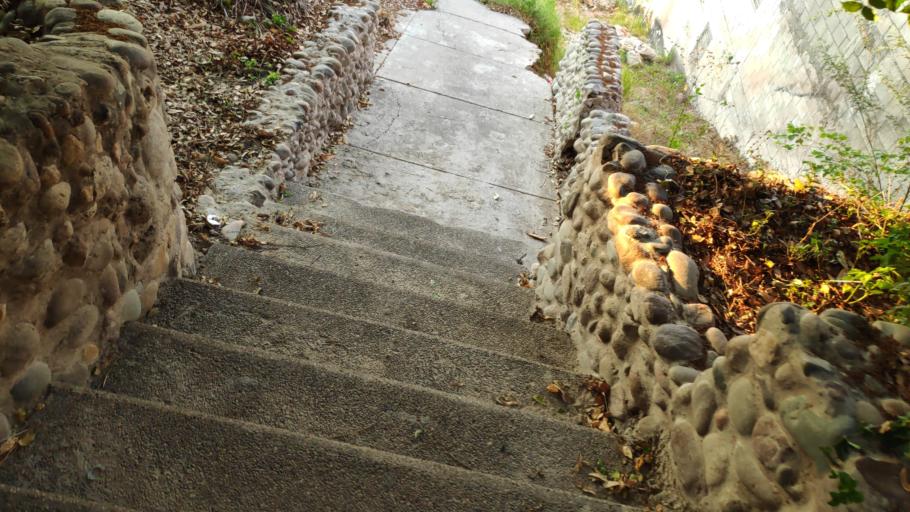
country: MX
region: Sinaloa
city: Culiacan
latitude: 24.7851
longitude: -107.4029
